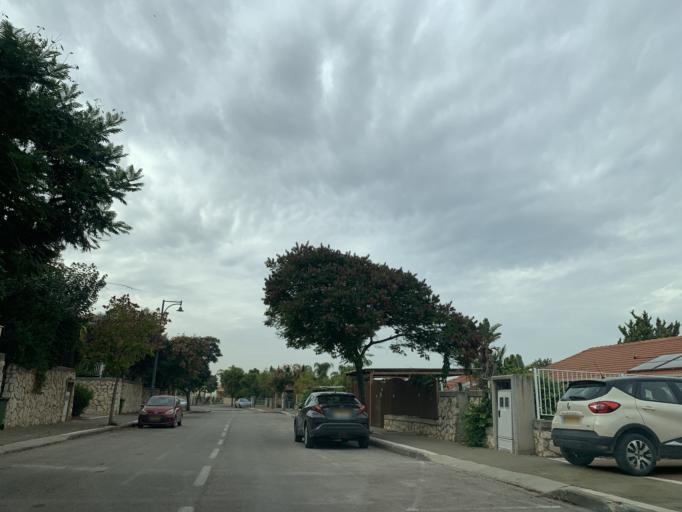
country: IL
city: Nirit
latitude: 32.1484
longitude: 34.9826
